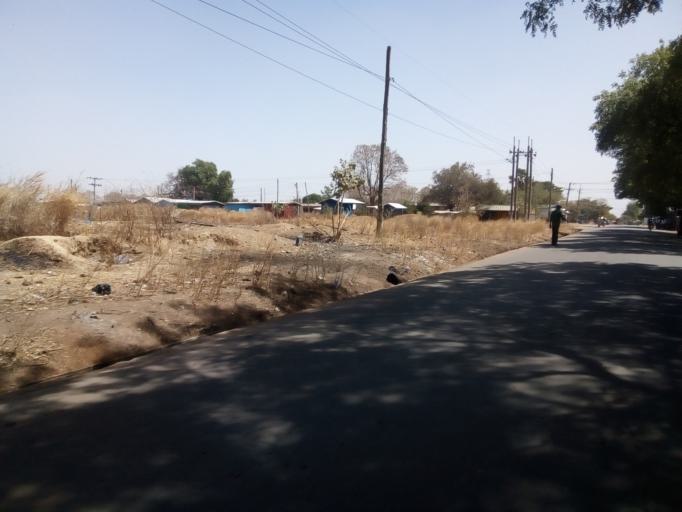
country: GH
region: Upper East
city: Navrongo
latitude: 10.8828
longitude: -1.0845
